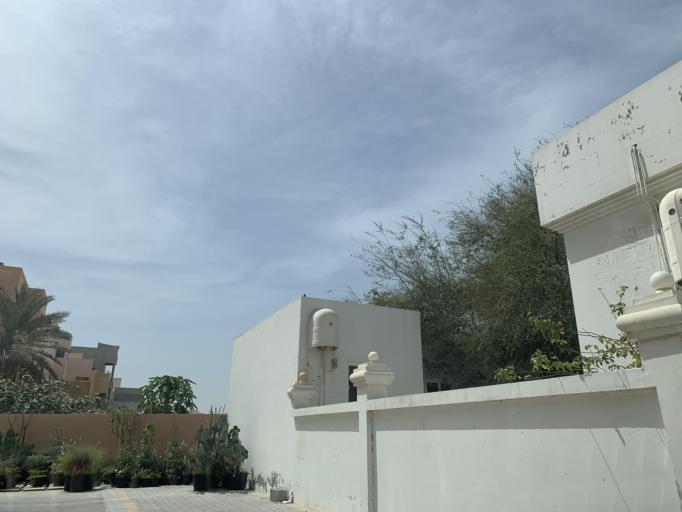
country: BH
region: Northern
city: Ar Rifa'
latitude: 26.1448
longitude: 50.5628
